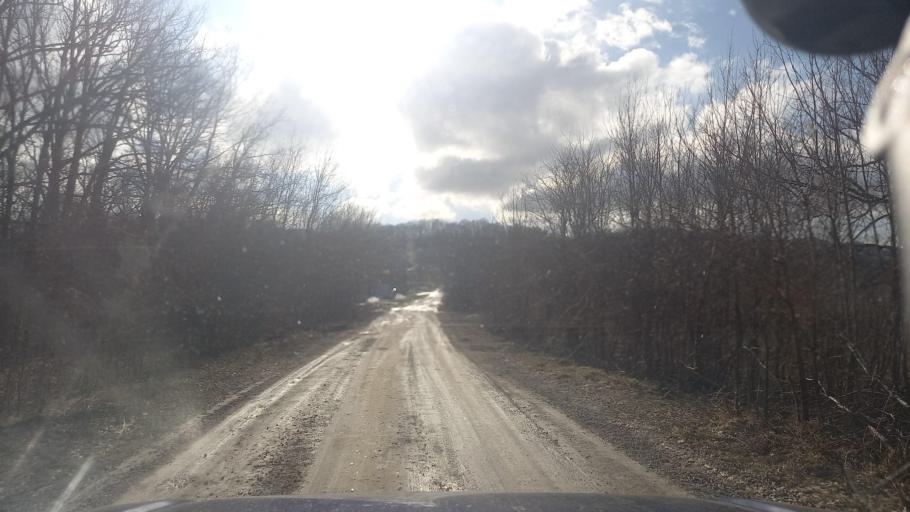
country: RU
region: Krasnodarskiy
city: Goryachiy Klyuch
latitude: 44.6895
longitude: 38.9834
